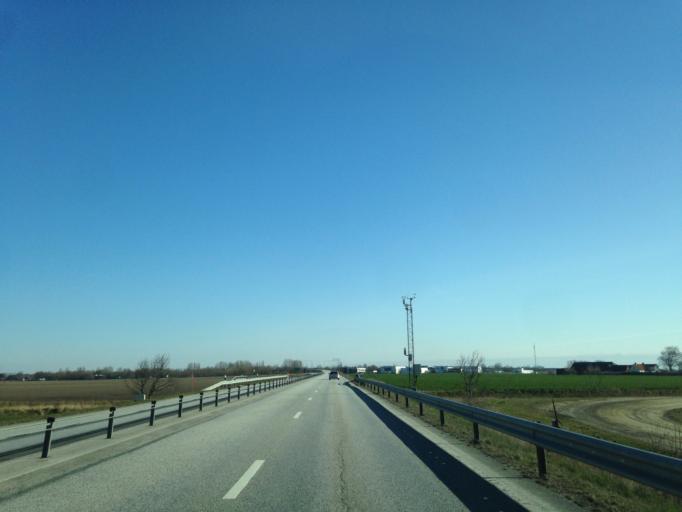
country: SE
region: Skane
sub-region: Vellinge Kommun
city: Vellinge
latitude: 55.4540
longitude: 13.0061
